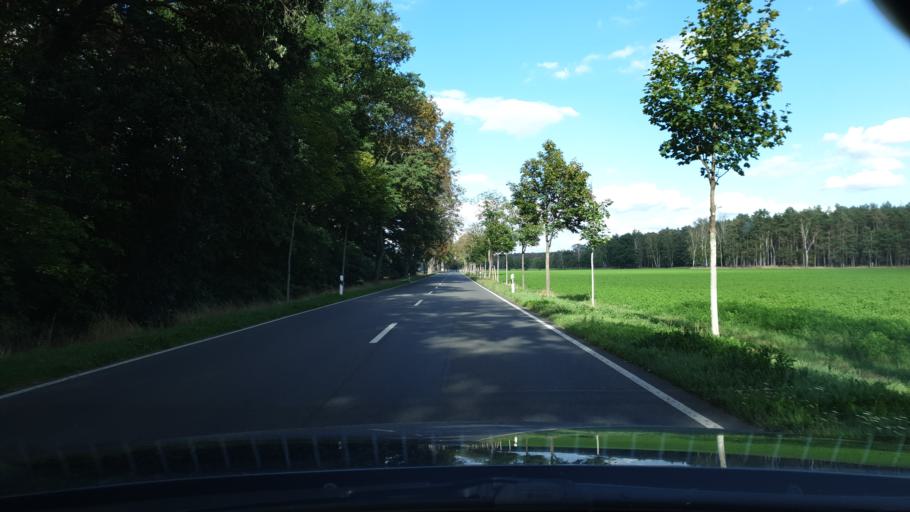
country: DE
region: Saxony-Anhalt
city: Radis
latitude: 51.7613
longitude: 12.5319
